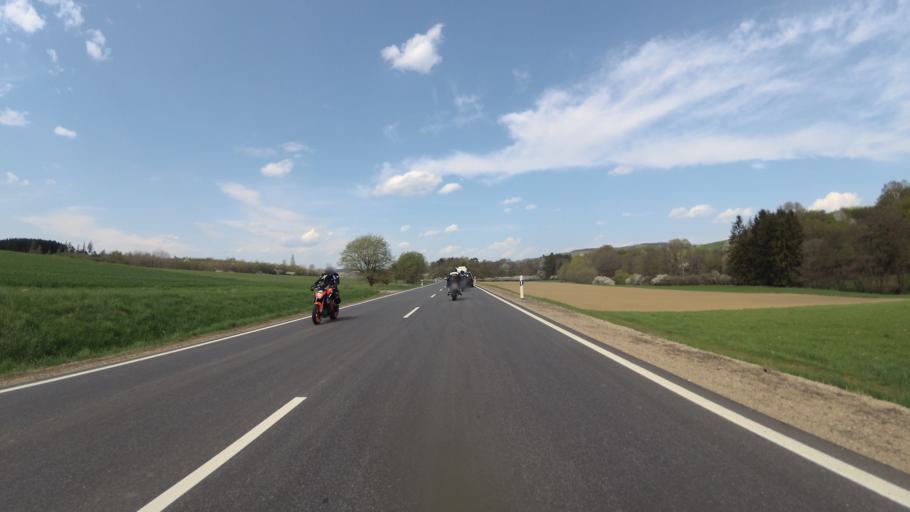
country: DE
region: Rheinland-Pfalz
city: Mullenbach
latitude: 50.3060
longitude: 6.9083
